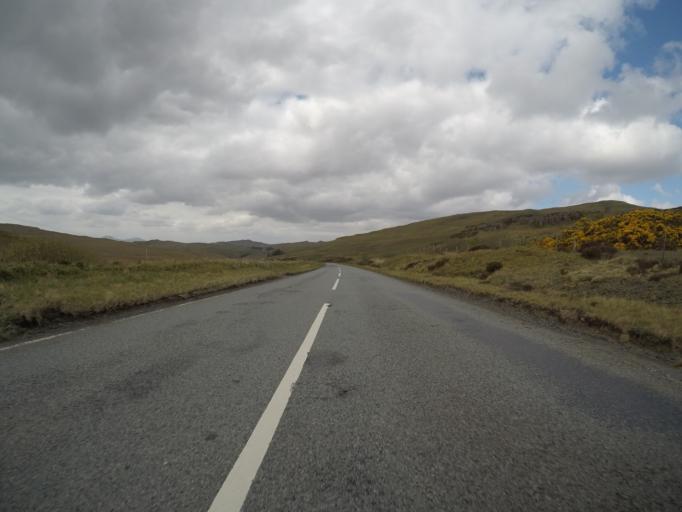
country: GB
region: Scotland
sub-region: Highland
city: Isle of Skye
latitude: 57.3176
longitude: -6.3218
